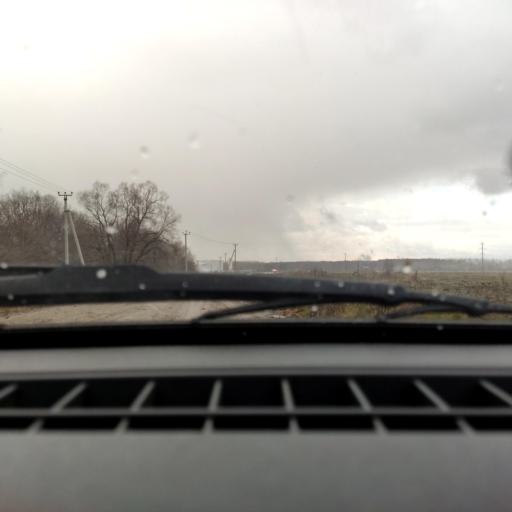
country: RU
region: Bashkortostan
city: Iglino
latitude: 54.7399
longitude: 56.3242
